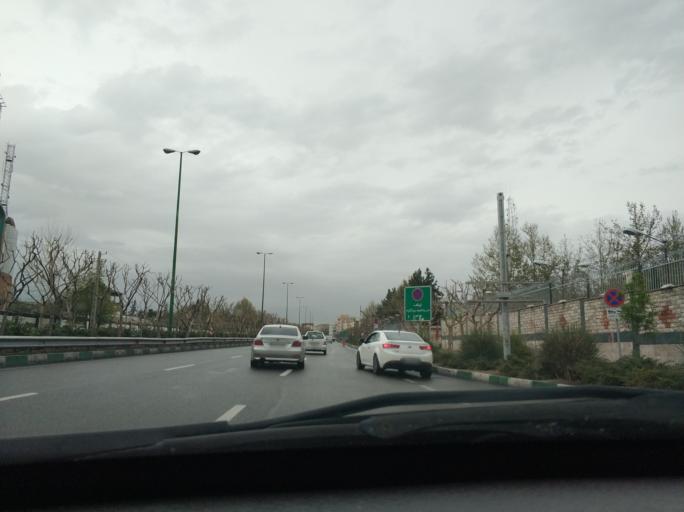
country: IR
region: Tehran
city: Tehran
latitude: 35.7072
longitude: 51.4406
